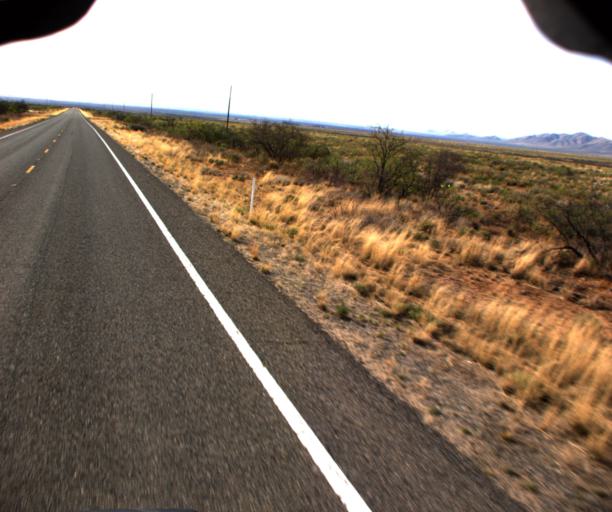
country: US
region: Arizona
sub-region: Cochise County
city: Willcox
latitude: 32.1870
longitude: -109.6794
